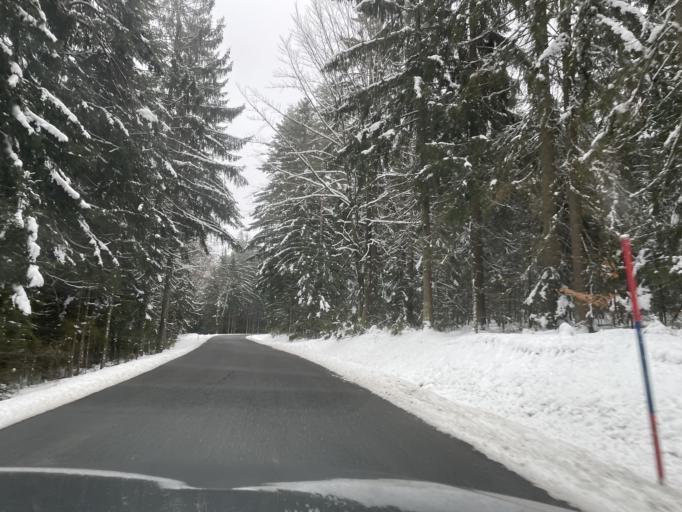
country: DE
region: Bavaria
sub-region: Lower Bavaria
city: Viechtach
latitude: 49.1363
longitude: 12.9118
